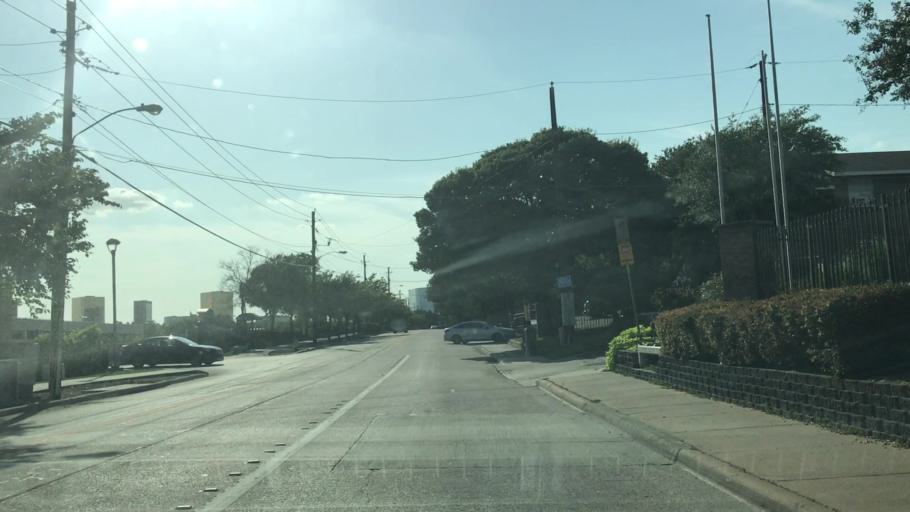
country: US
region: Texas
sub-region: Dallas County
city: University Park
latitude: 32.8642
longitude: -96.7524
